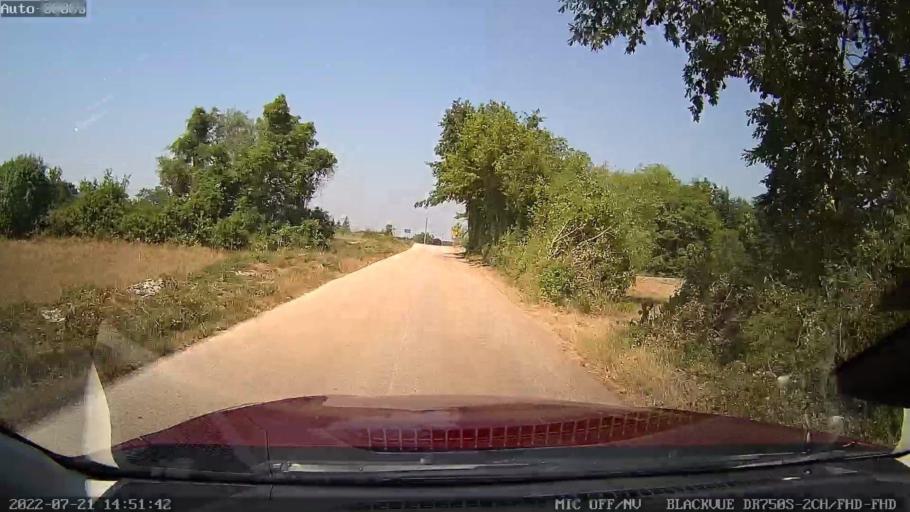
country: HR
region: Istarska
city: Pazin
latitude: 45.1709
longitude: 13.9250
